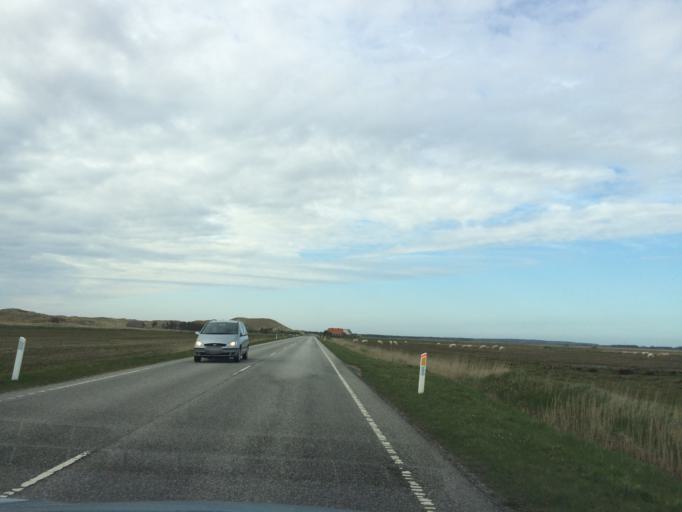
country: DK
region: Central Jutland
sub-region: Ringkobing-Skjern Kommune
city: Ringkobing
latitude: 56.2261
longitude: 8.1399
